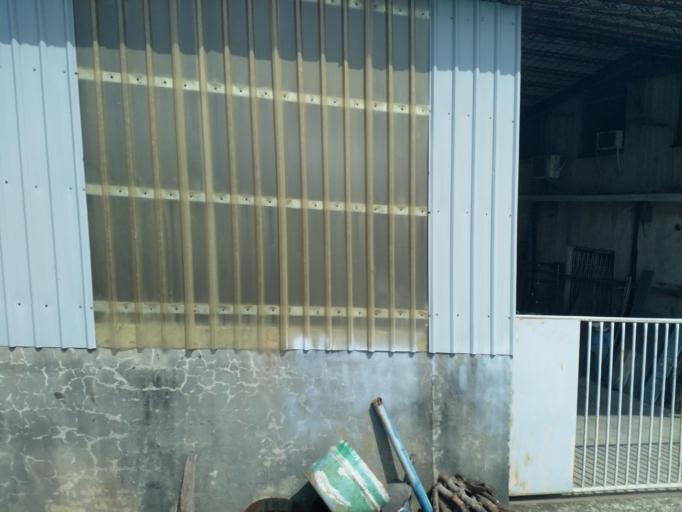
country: TW
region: Taiwan
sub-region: Pingtung
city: Pingtung
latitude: 22.8764
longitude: 120.5726
